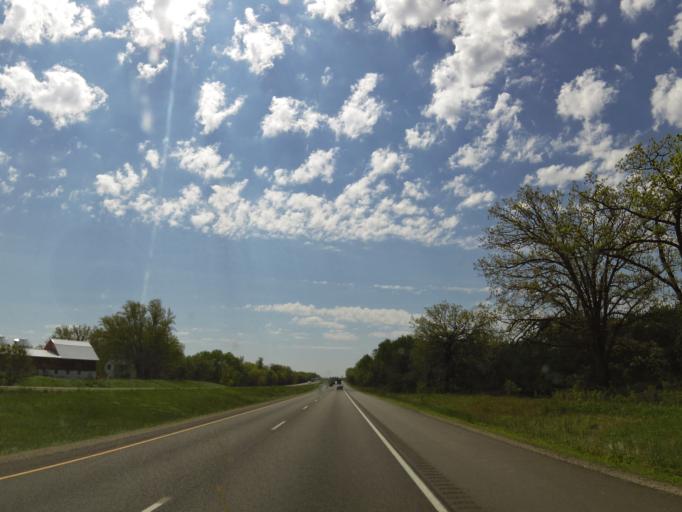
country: US
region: Wisconsin
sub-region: Eau Claire County
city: Fall Creek
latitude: 44.6844
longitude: -91.3308
